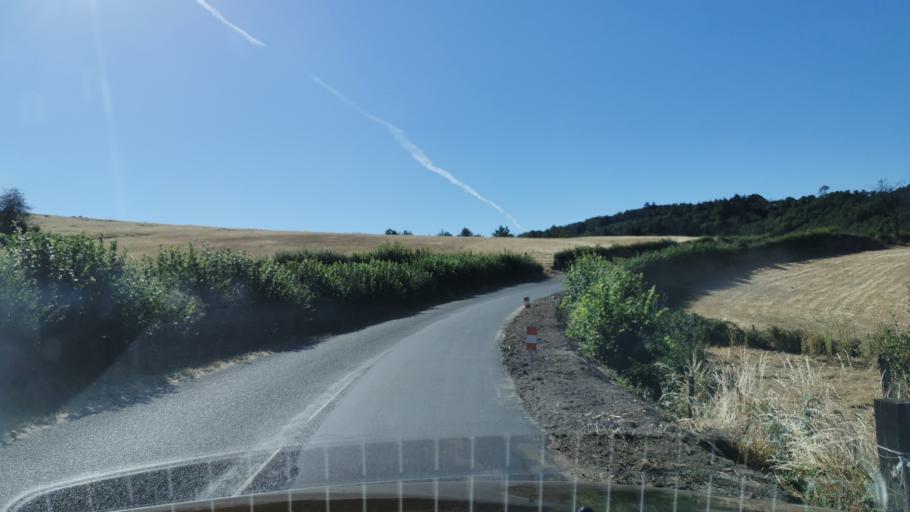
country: FR
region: Bourgogne
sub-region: Departement de Saone-et-Loire
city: Marmagne
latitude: 46.8041
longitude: 4.3456
